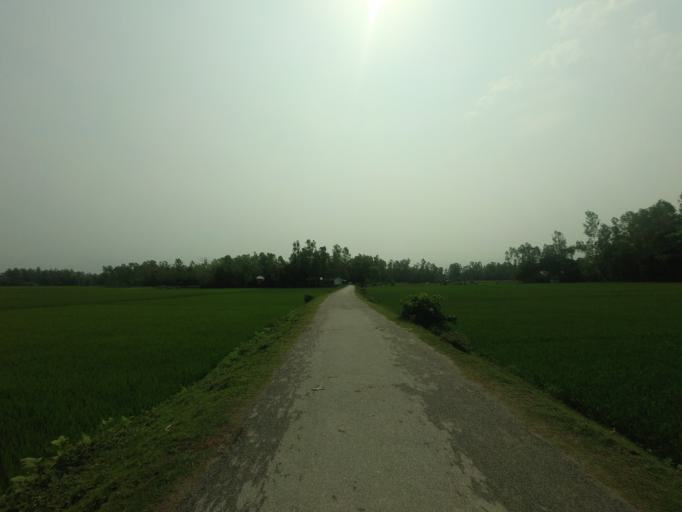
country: BD
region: Rajshahi
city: Sirajganj
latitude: 24.3214
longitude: 89.6772
